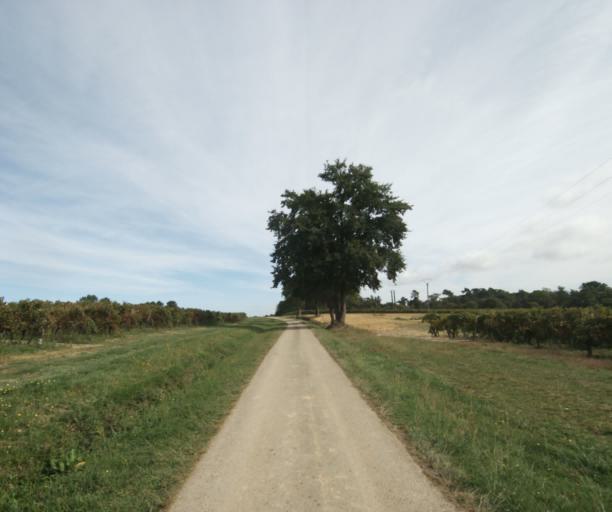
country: FR
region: Midi-Pyrenees
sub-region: Departement du Gers
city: Eauze
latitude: 43.8581
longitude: 0.1390
